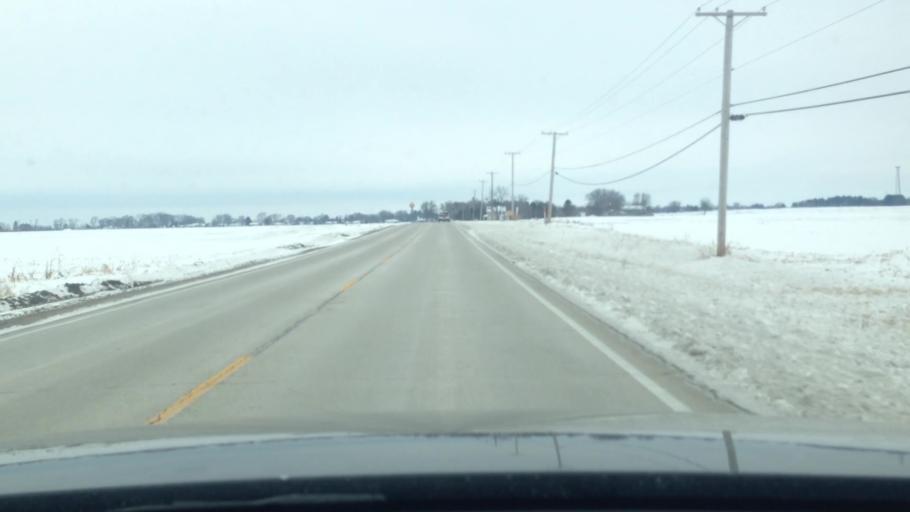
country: US
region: Illinois
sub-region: McHenry County
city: Hebron
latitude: 42.4517
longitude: -88.4330
